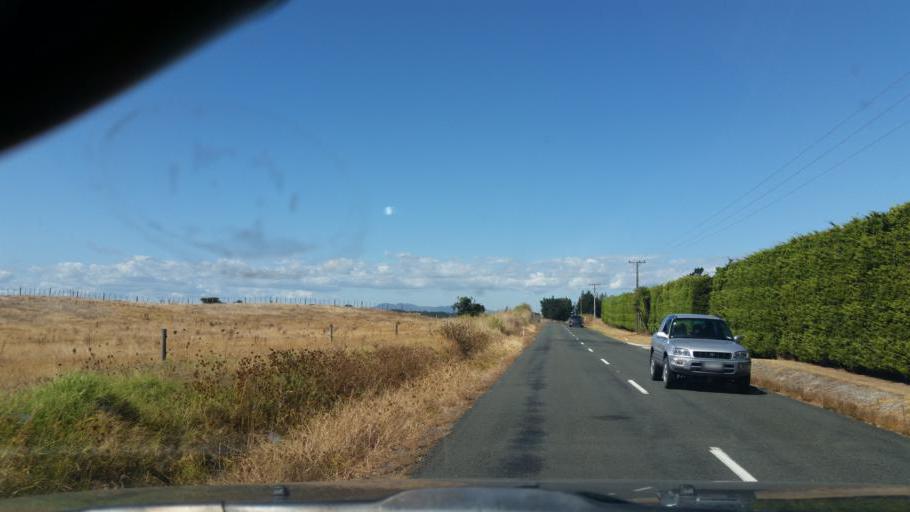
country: NZ
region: Northland
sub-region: Kaipara District
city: Dargaville
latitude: -35.9444
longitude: 173.8208
